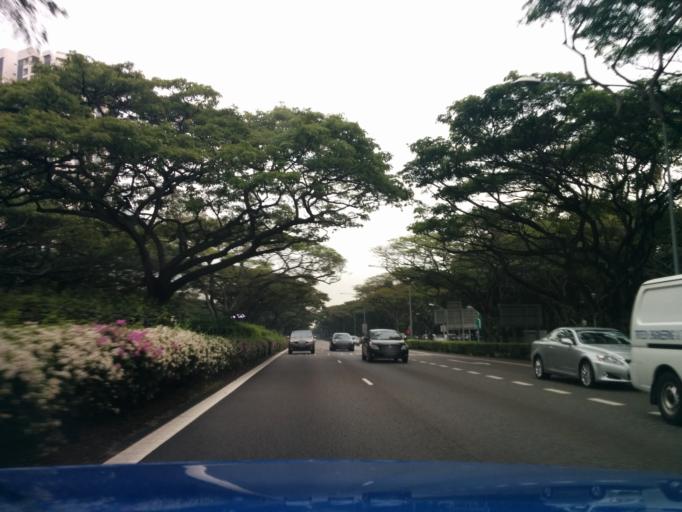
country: SG
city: Singapore
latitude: 1.3094
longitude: 103.9362
